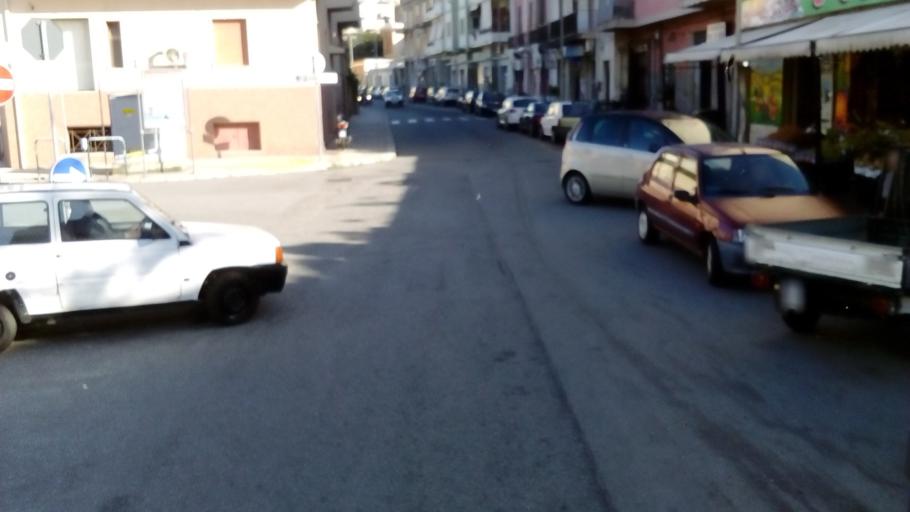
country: IT
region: Calabria
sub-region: Provincia di Reggio Calabria
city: Campo Calabro
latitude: 38.2122
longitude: 15.6371
